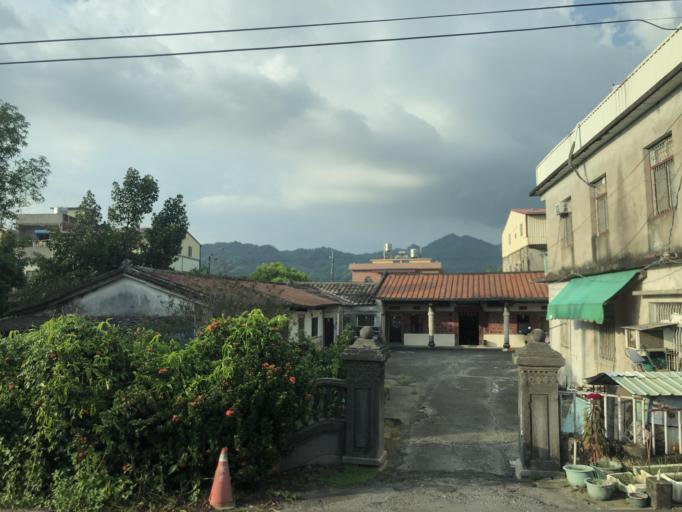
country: TW
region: Taiwan
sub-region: Pingtung
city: Pingtung
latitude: 22.8867
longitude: 120.5294
